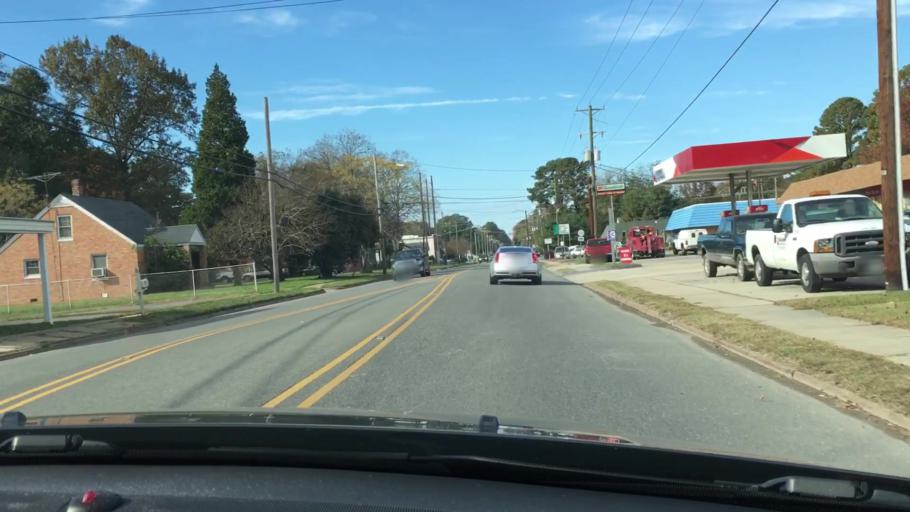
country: US
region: Virginia
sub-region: King William County
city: West Point
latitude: 37.5515
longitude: -76.8104
